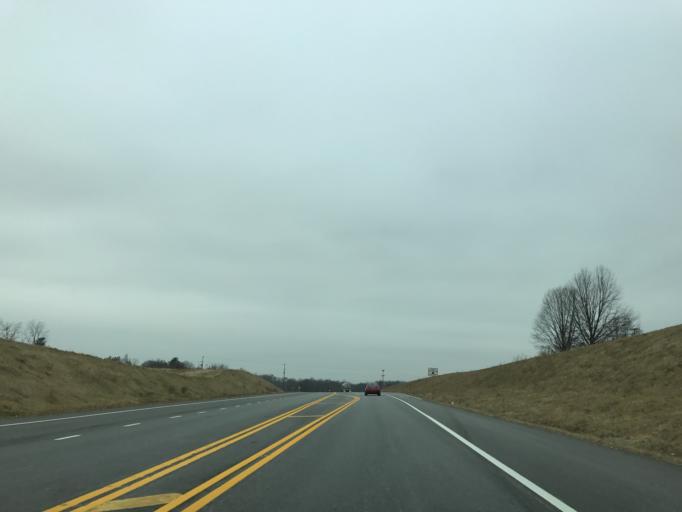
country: US
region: Maryland
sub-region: Carroll County
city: Westminster
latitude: 39.6059
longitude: -77.0596
